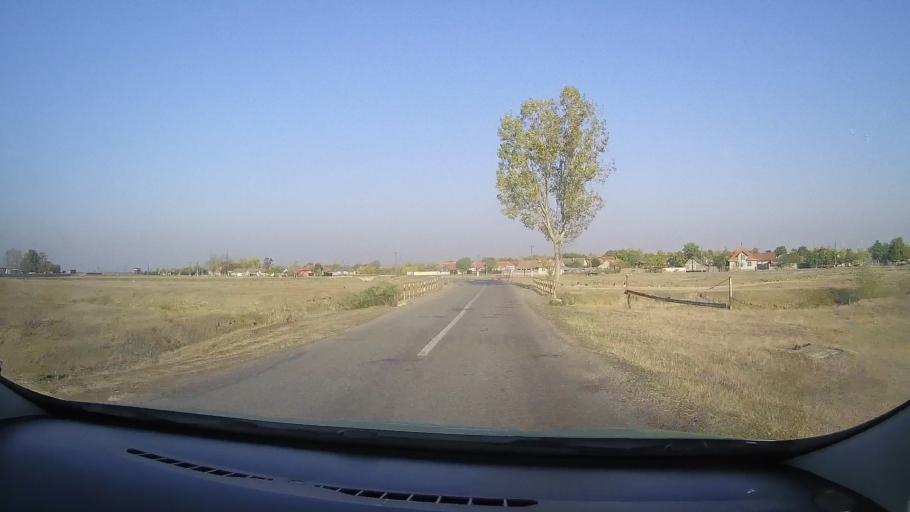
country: RO
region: Arad
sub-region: Comuna Graniceri
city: Graniceri
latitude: 46.5138
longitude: 21.3076
